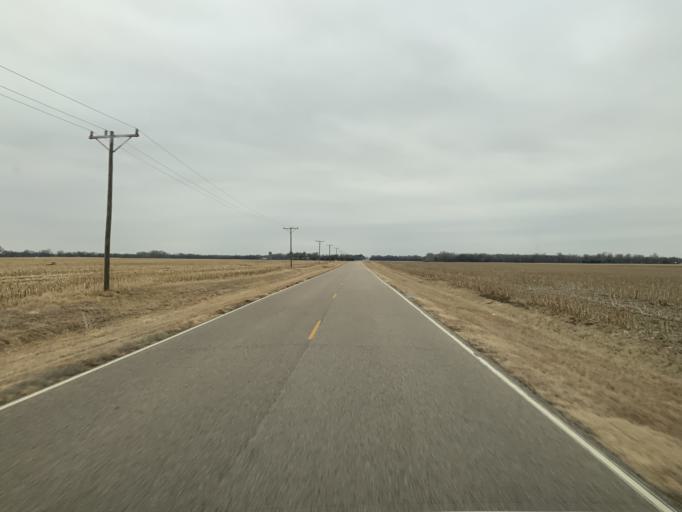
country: US
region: Kansas
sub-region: Reno County
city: South Hutchinson
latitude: 37.9519
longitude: -98.0874
